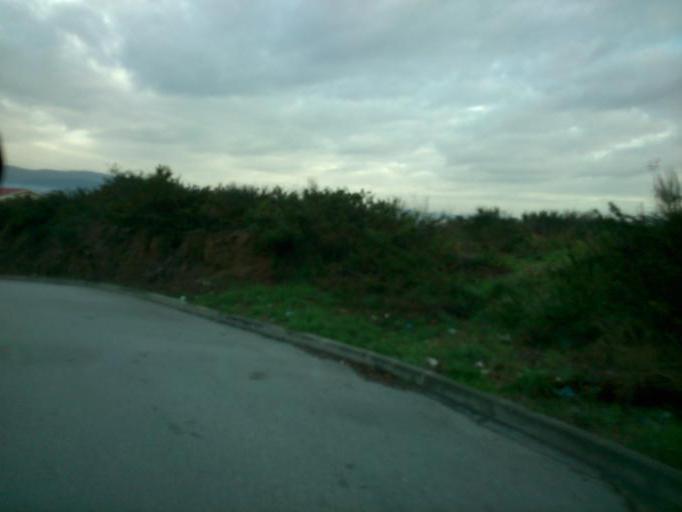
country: PT
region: Braga
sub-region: Barcelos
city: Barcelos
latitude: 41.5205
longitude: -8.6072
